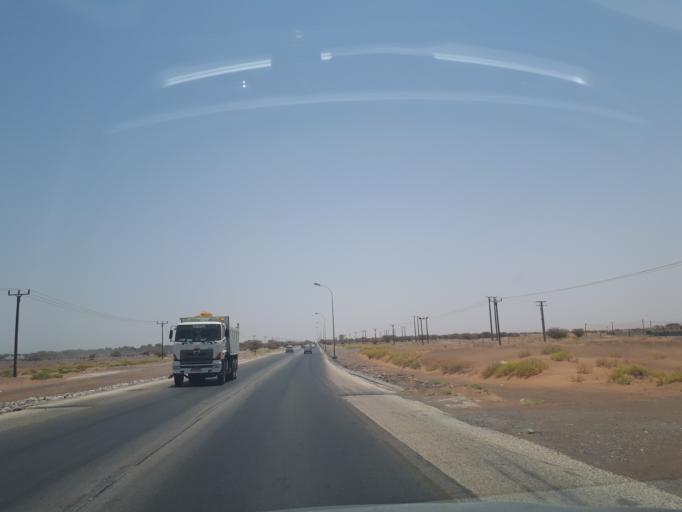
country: OM
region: Ash Sharqiyah
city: Badiyah
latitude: 22.4859
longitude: 58.7750
